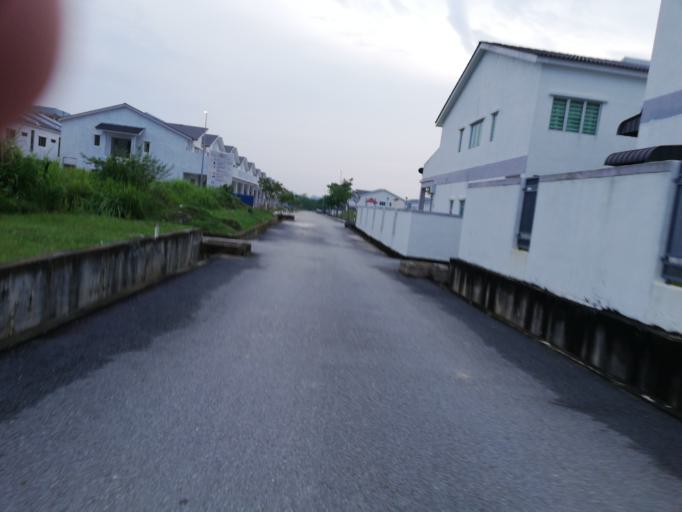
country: MY
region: Kedah
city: Kulim
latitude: 5.3846
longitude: 100.5828
